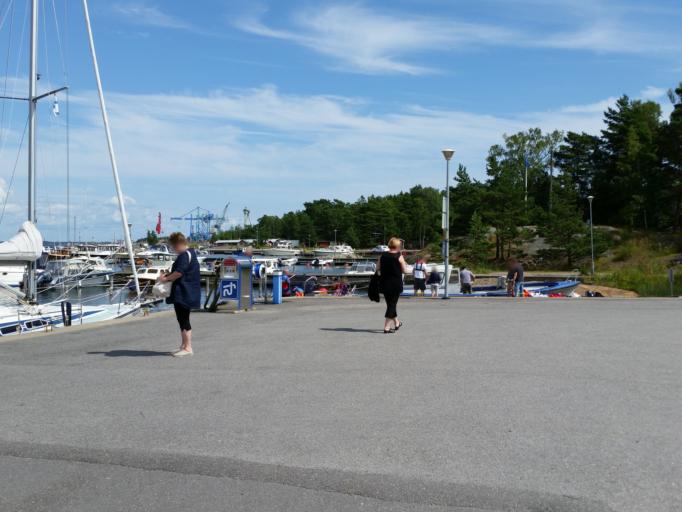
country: FI
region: Uusimaa
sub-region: Raaseporin
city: Hanko
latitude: 59.8423
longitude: 22.9476
